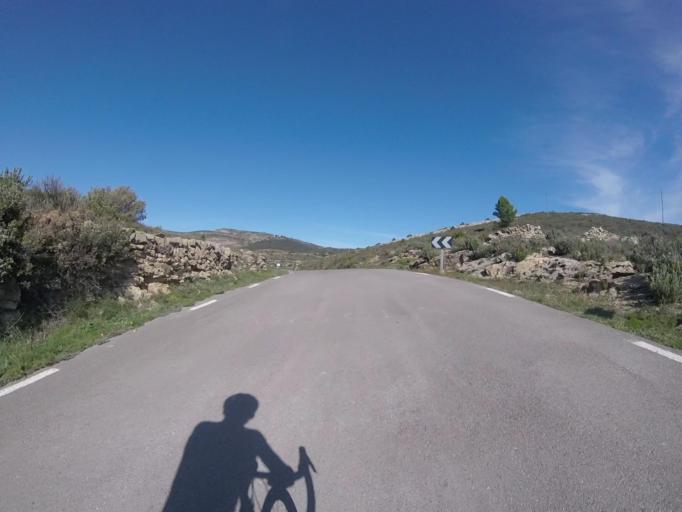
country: ES
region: Valencia
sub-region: Provincia de Castello
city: Sarratella
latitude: 40.2926
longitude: 0.0313
